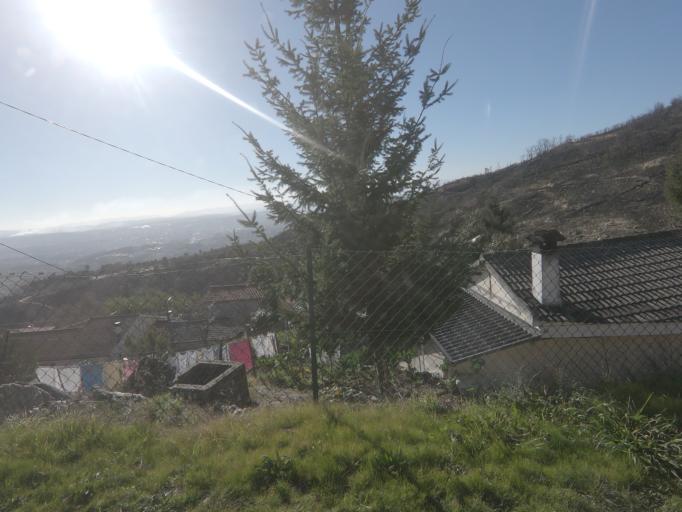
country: PT
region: Vila Real
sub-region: Vila Real
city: Vila Real
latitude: 41.3507
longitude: -7.7478
